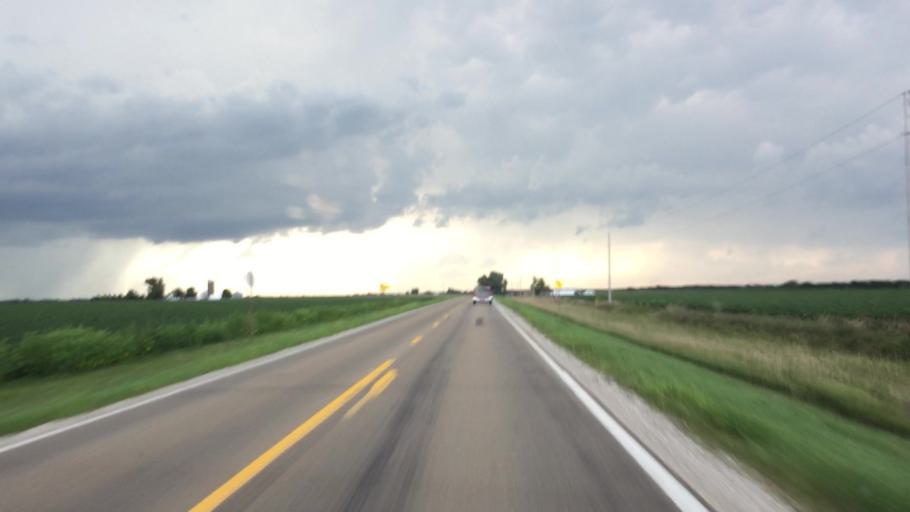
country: US
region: Iowa
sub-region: Henry County
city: New London
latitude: 40.7781
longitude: -91.4778
